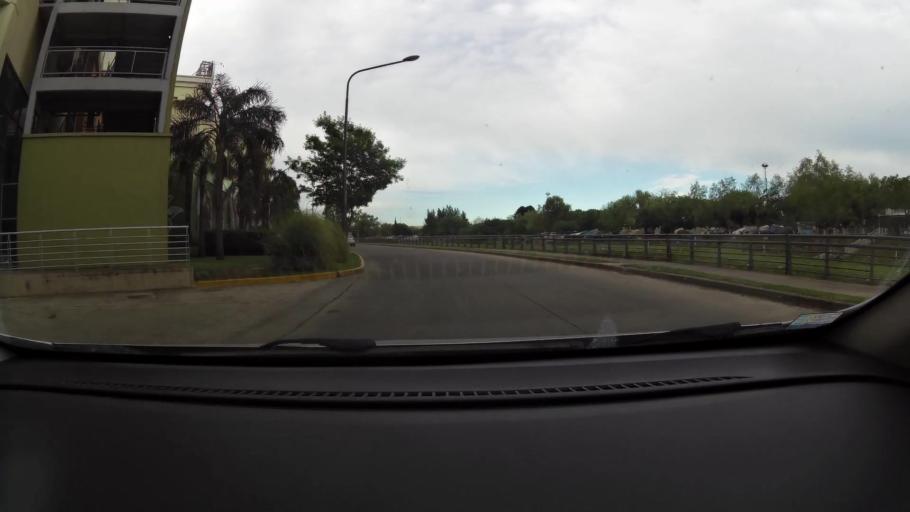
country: AR
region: Santa Fe
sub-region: Departamento de Rosario
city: Rosario
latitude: -32.9108
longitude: -60.6824
